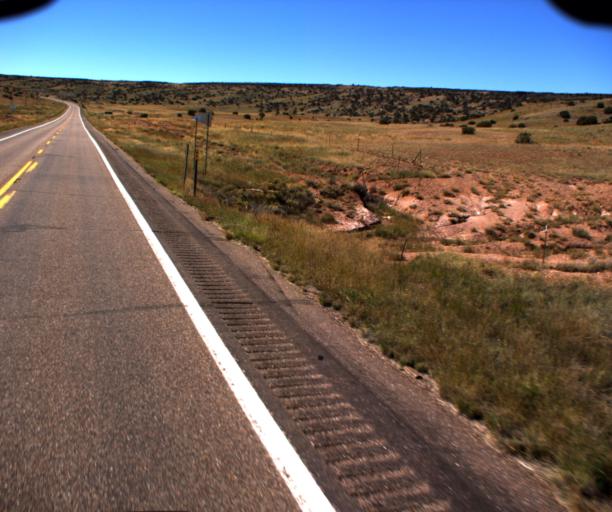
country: US
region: Arizona
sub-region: Apache County
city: Saint Johns
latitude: 34.3449
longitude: -109.3811
